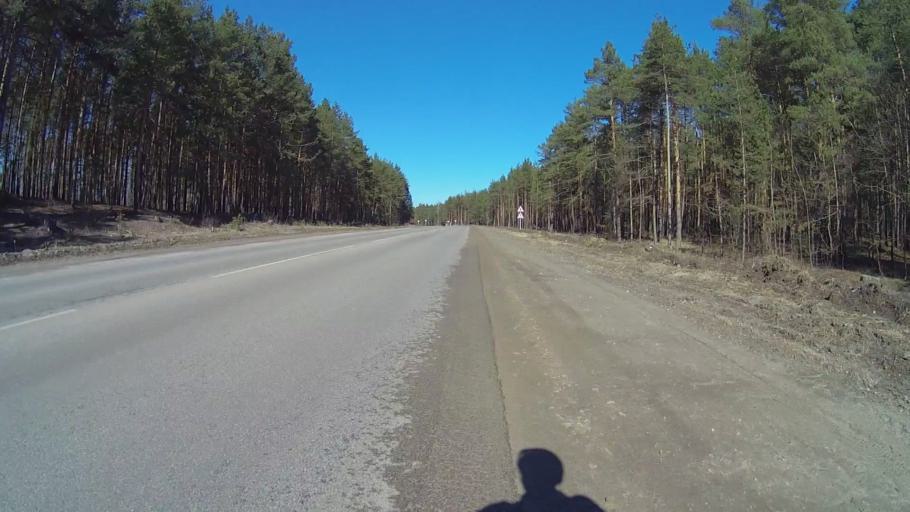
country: RU
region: Vladimir
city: Kommunar
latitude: 56.0701
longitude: 40.4326
